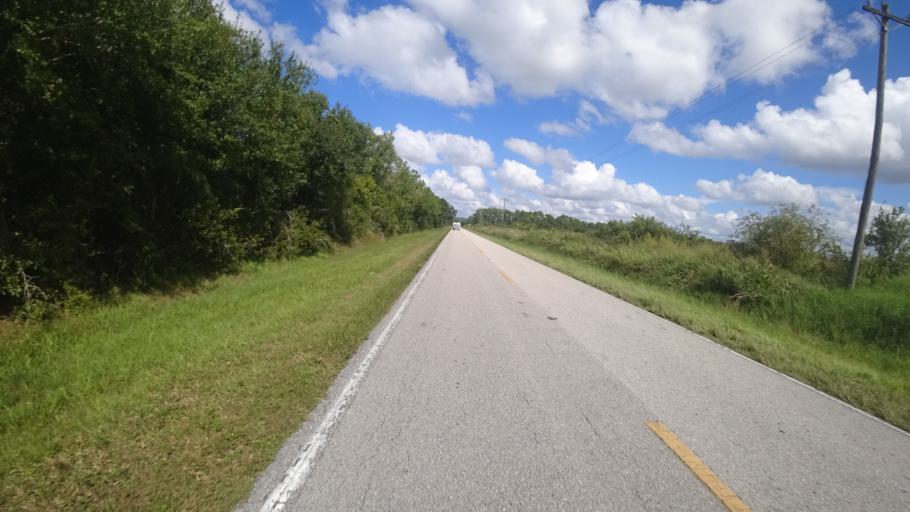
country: US
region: Florida
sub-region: Sarasota County
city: Lake Sarasota
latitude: 27.3785
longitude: -82.1400
